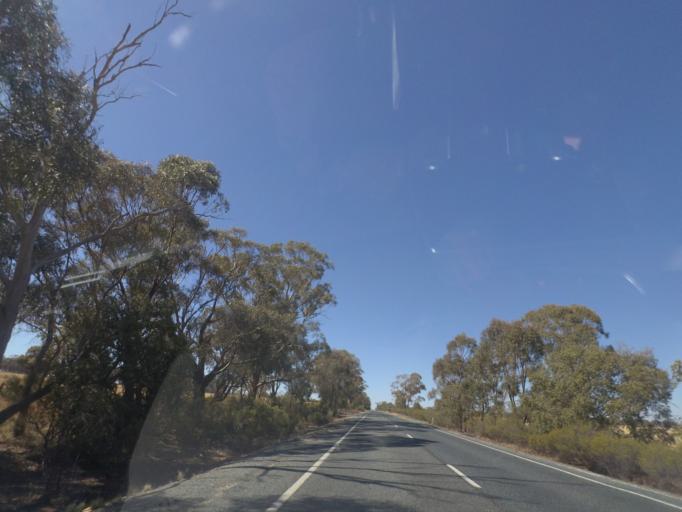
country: AU
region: New South Wales
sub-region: Bland
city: West Wyalong
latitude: -34.1597
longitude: 147.1170
